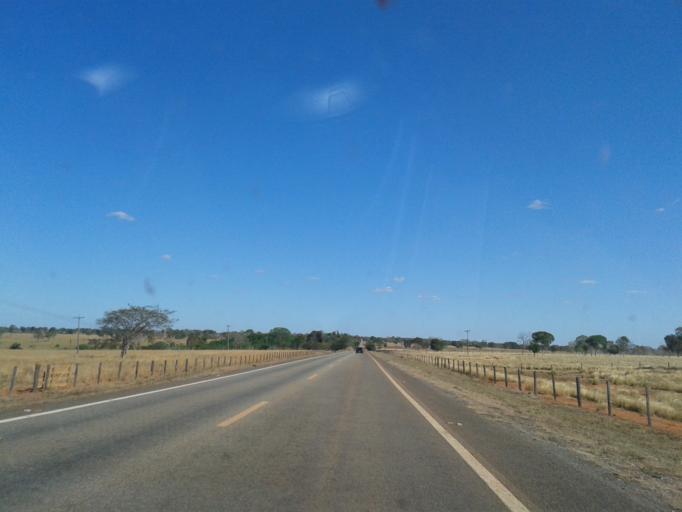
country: BR
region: Goias
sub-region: Mozarlandia
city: Mozarlandia
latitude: -14.2676
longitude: -50.3992
